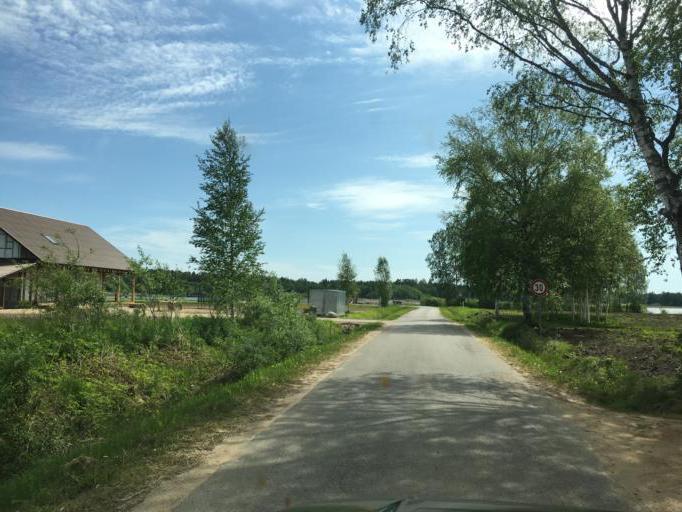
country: LV
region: Talsu Rajons
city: Valdemarpils
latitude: 57.3666
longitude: 22.6036
